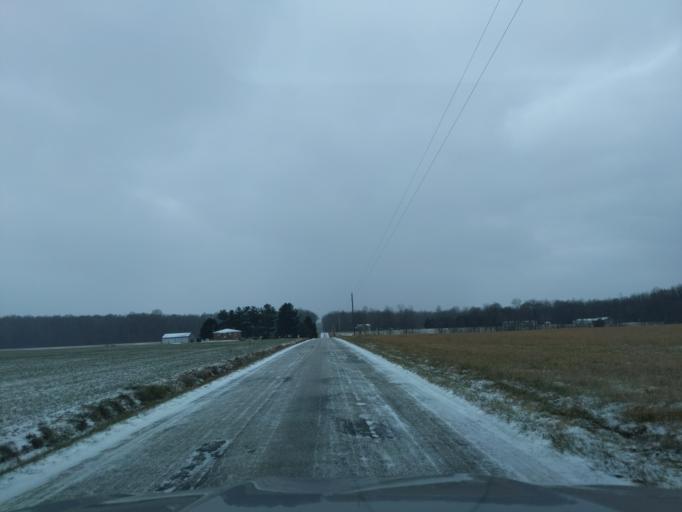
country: US
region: Indiana
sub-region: Decatur County
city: Greensburg
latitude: 39.2338
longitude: -85.4796
